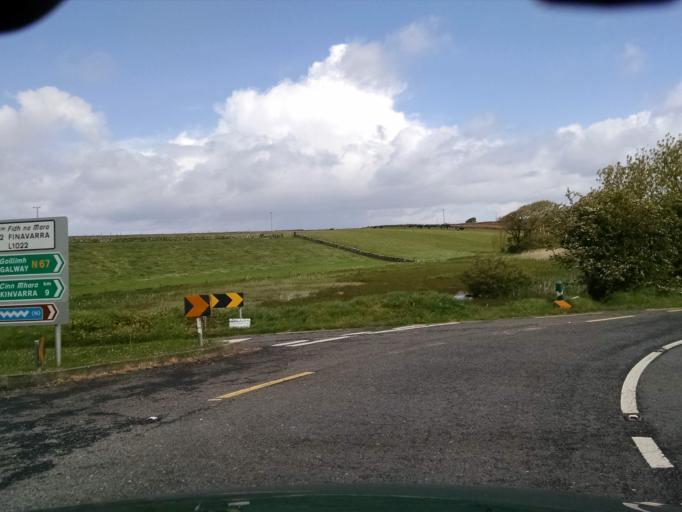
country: IE
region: Connaught
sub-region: County Galway
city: Bearna
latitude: 53.1467
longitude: -9.0801
